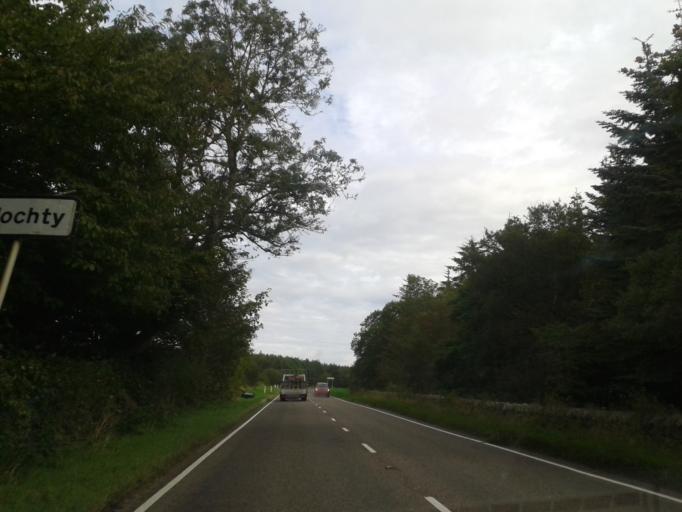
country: GB
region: Scotland
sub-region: Moray
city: Findochty
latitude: 57.6828
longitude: -2.8881
